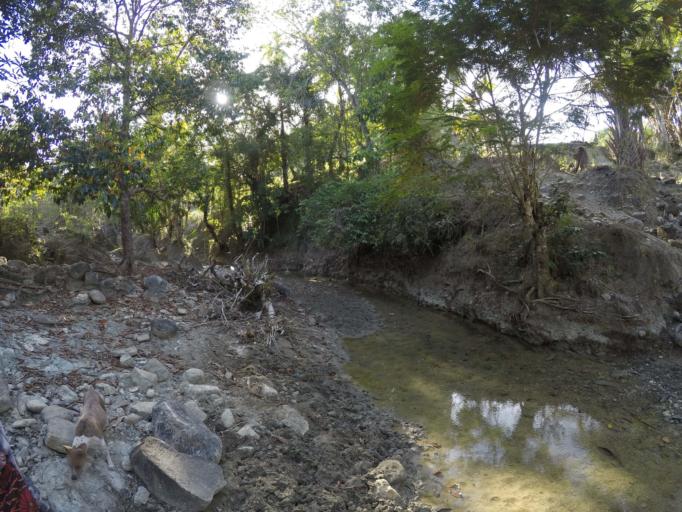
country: TL
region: Viqueque
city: Viqueque
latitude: -8.8348
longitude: 126.3789
